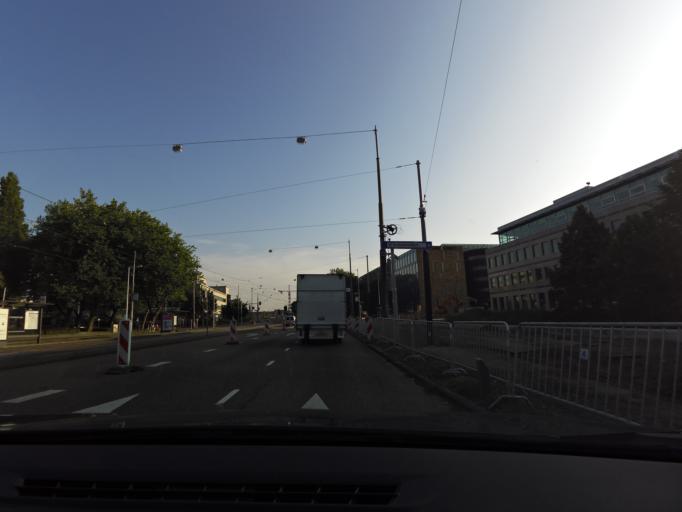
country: NL
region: North Holland
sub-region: Gemeente Amstelveen
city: Amstelveen
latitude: 52.3403
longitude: 4.8578
